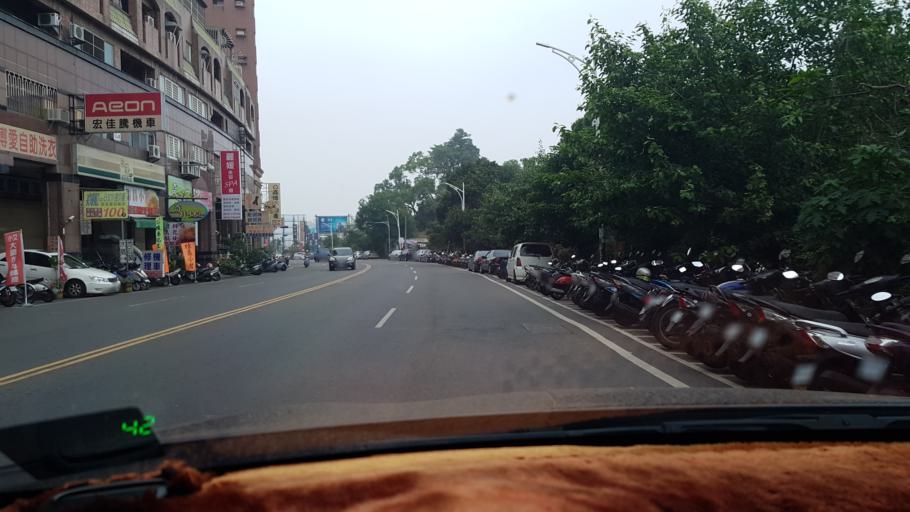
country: TW
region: Taiwan
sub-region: Chiayi
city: Jiayi Shi
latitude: 23.4907
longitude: 120.4612
